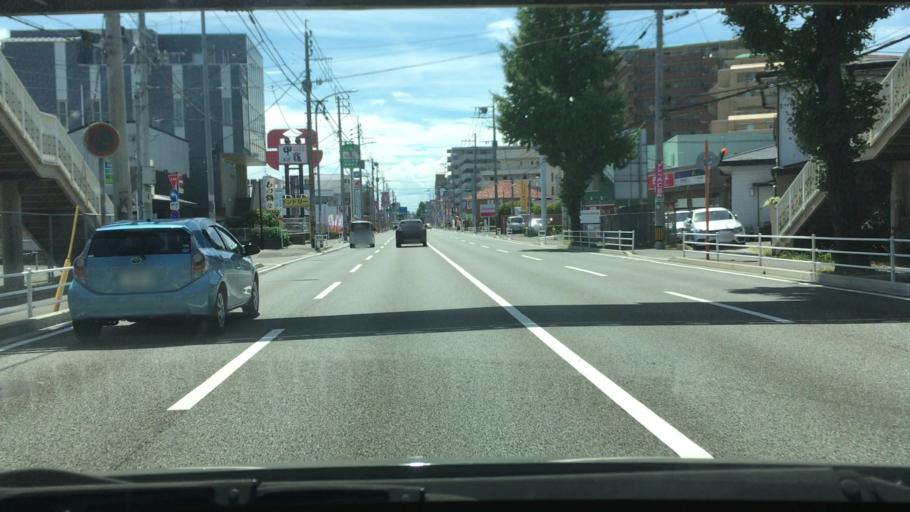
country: JP
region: Fukuoka
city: Onojo
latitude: 33.5636
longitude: 130.4448
